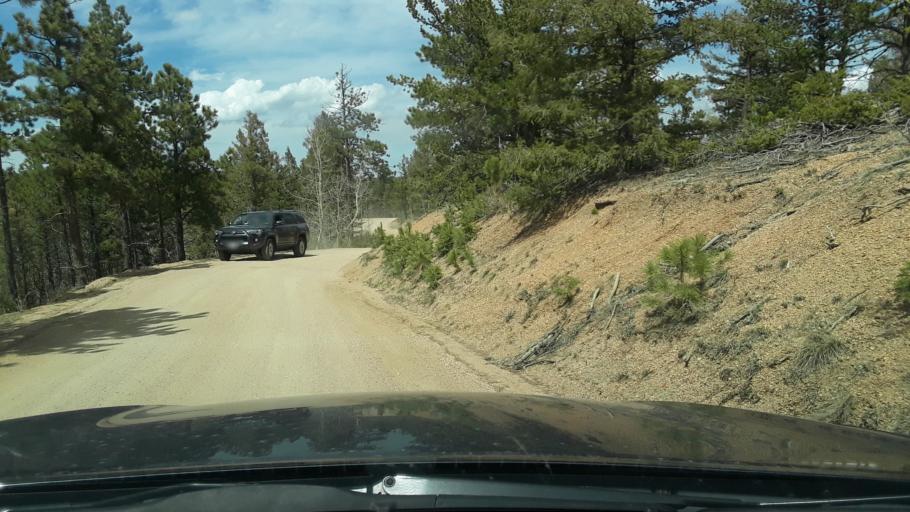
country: US
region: Colorado
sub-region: El Paso County
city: Palmer Lake
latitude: 39.0673
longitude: -104.9641
